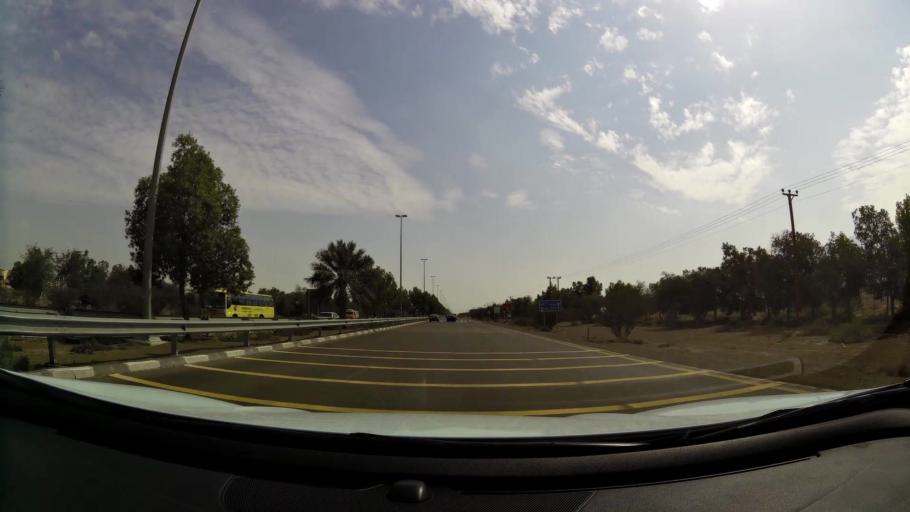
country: AE
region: Abu Dhabi
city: Al Ain
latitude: 24.1083
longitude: 55.8261
